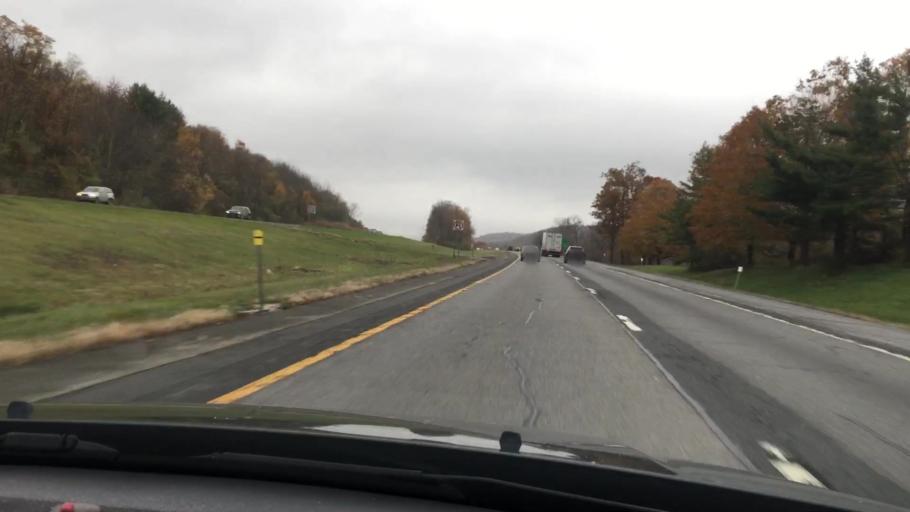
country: US
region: New York
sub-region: Putnam County
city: Lake Carmel
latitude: 41.4681
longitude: -73.6452
